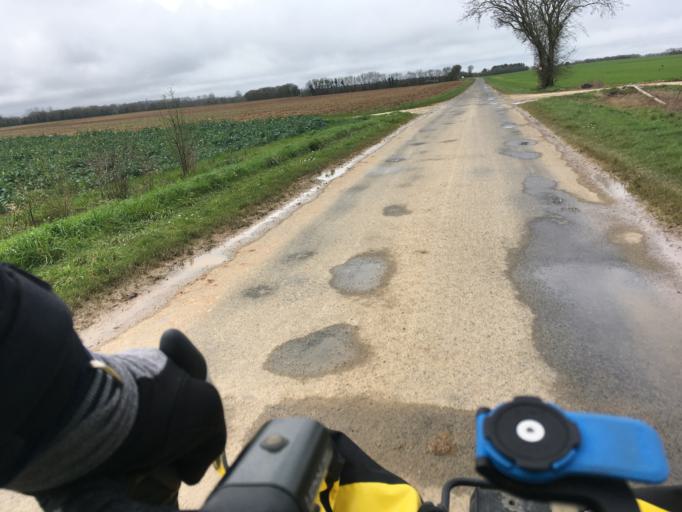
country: FR
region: Poitou-Charentes
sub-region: Departement de la Charente-Maritime
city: Saint-Germain-de-Marencennes
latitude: 46.1203
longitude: -0.8375
